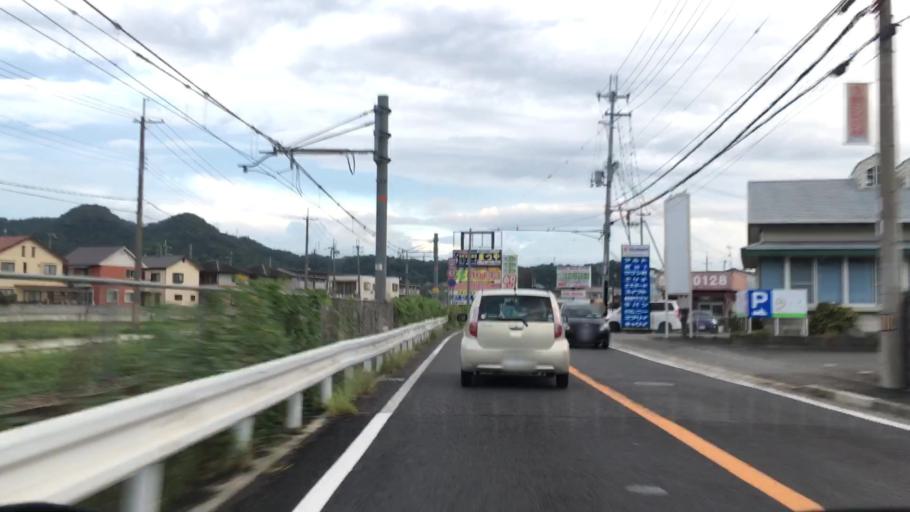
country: JP
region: Hyogo
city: Himeji
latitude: 34.8795
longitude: 134.7288
